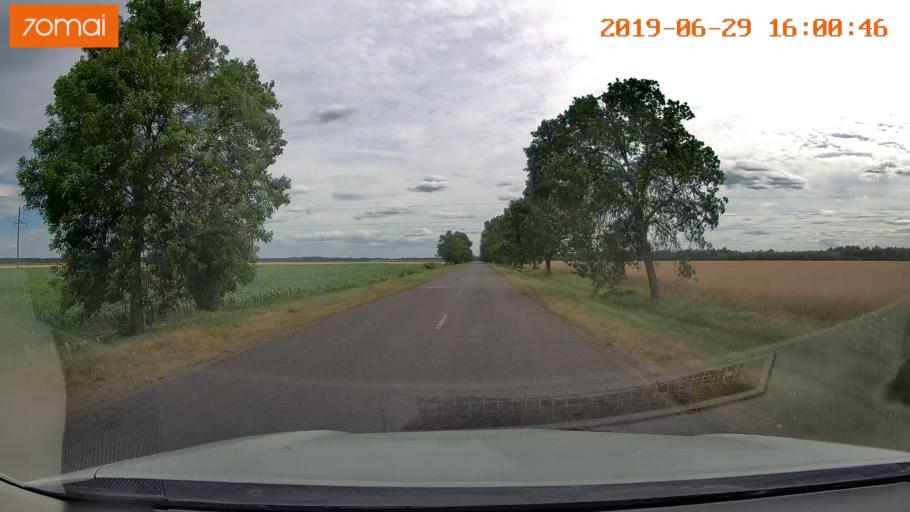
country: BY
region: Brest
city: Luninyets
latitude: 52.2561
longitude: 27.0172
